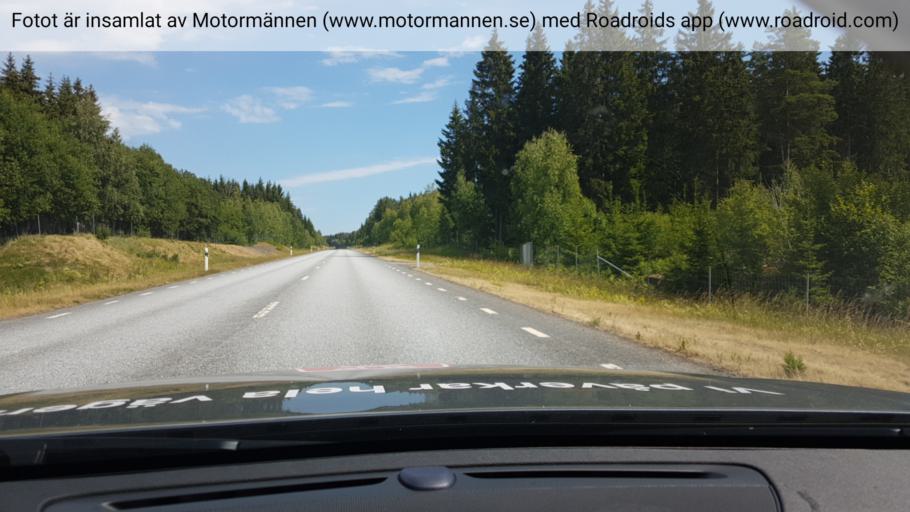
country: SE
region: Uppsala
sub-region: Osthammars Kommun
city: Gimo
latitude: 60.1660
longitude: 18.2161
